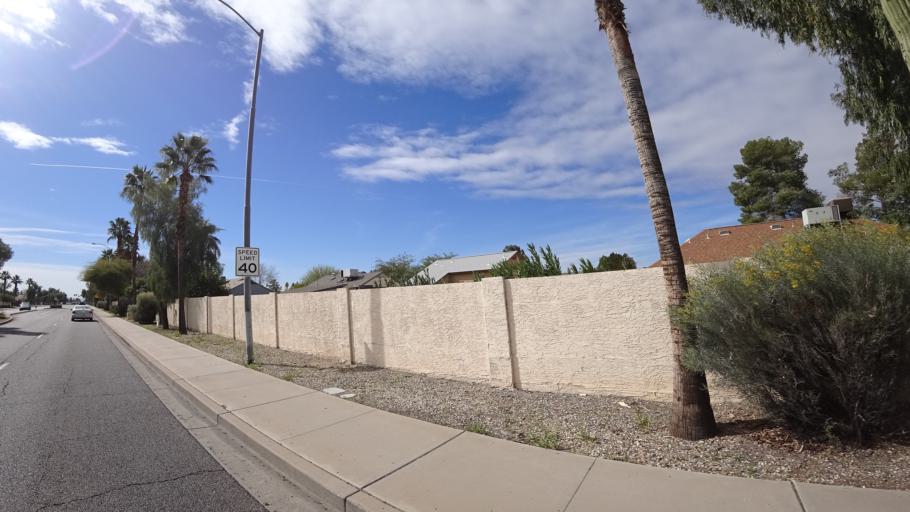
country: US
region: Arizona
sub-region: Maricopa County
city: Peoria
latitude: 33.6166
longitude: -112.1859
